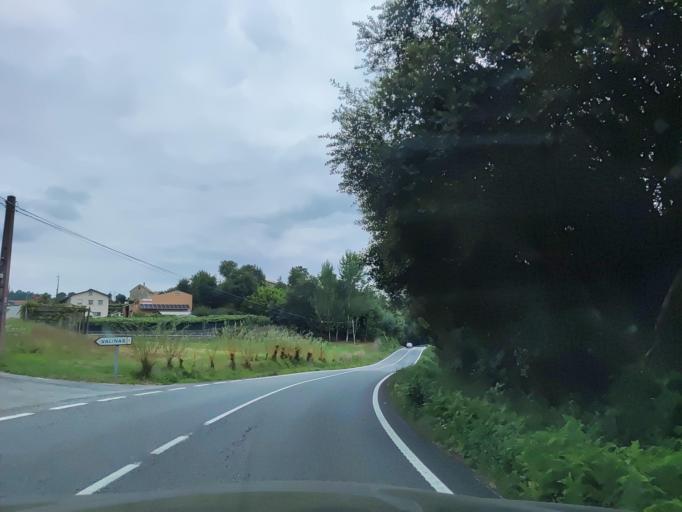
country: ES
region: Galicia
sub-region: Provincia da Coruna
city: Teo
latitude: 42.7563
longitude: -8.5612
